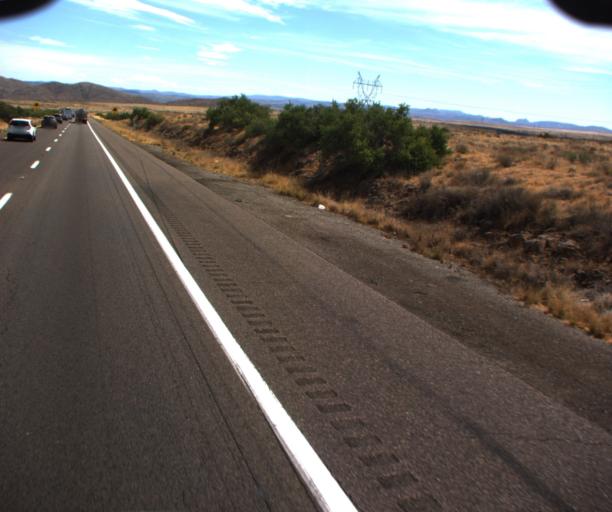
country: US
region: Arizona
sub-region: Yavapai County
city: Cordes Lakes
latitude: 34.2101
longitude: -112.1165
